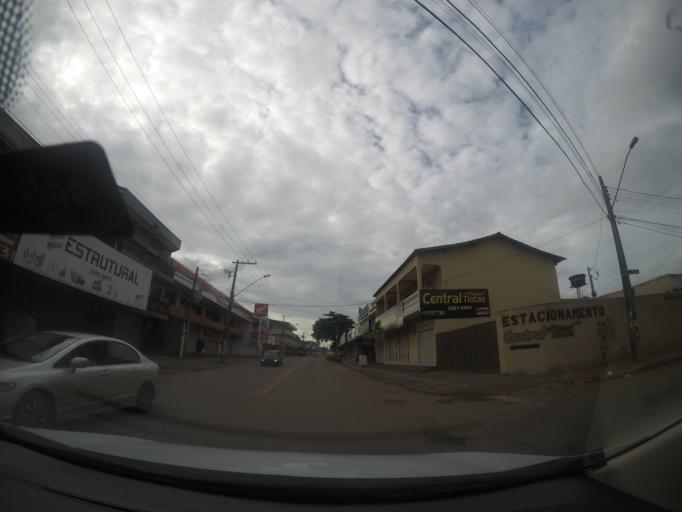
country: BR
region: Goias
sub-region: Goiania
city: Goiania
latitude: -16.6479
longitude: -49.3220
